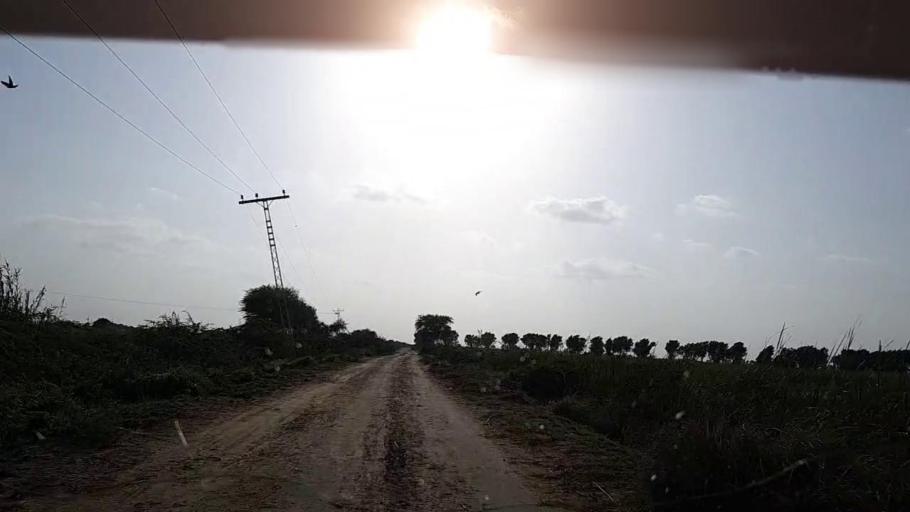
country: PK
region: Sindh
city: Badin
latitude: 24.5592
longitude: 68.8947
